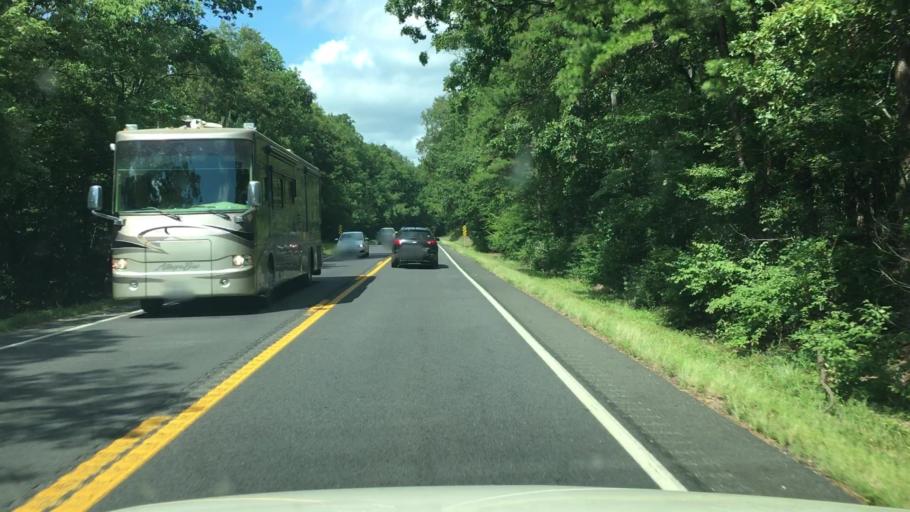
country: US
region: Arkansas
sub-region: Garland County
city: Lake Hamilton
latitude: 34.3611
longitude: -93.1694
